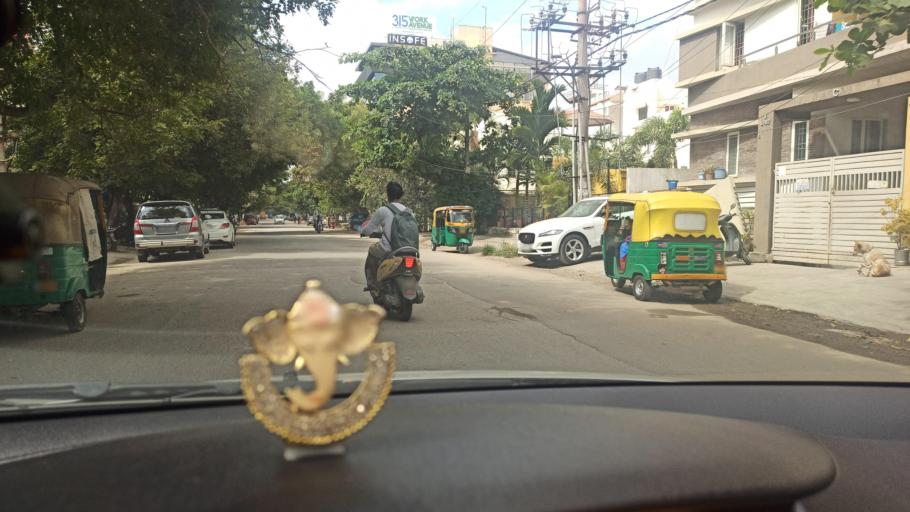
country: IN
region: Karnataka
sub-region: Bangalore Urban
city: Bangalore
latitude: 12.9139
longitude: 77.6315
